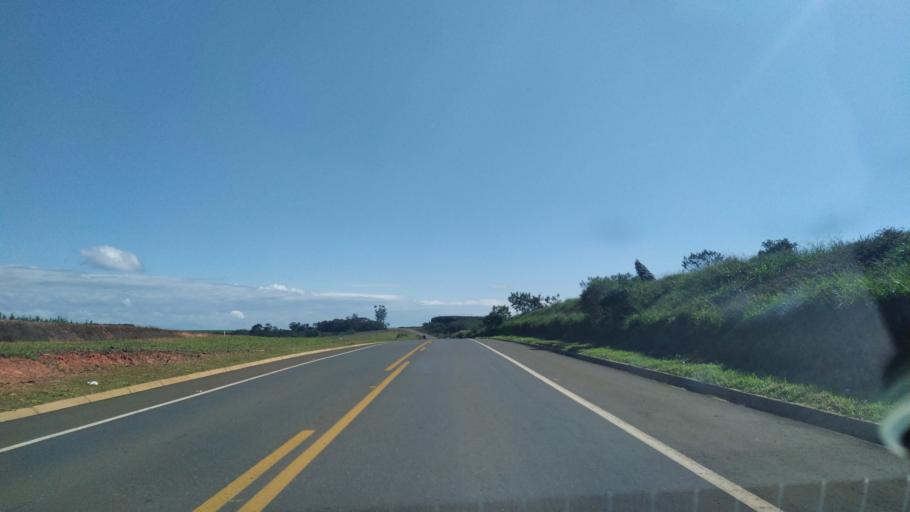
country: BR
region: Parana
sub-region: Ortigueira
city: Ortigueira
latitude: -24.2566
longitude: -50.7925
